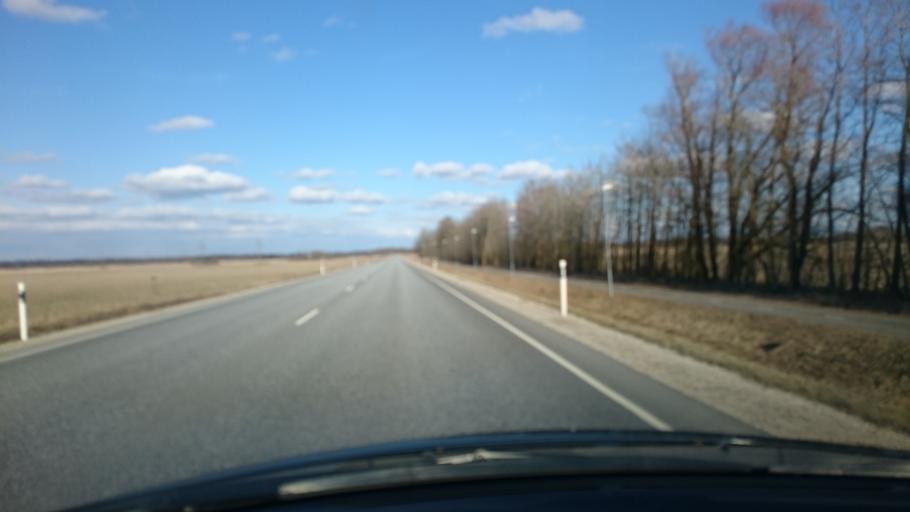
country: EE
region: Laeaene
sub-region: Lihula vald
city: Lihula
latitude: 58.7283
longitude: 23.9631
